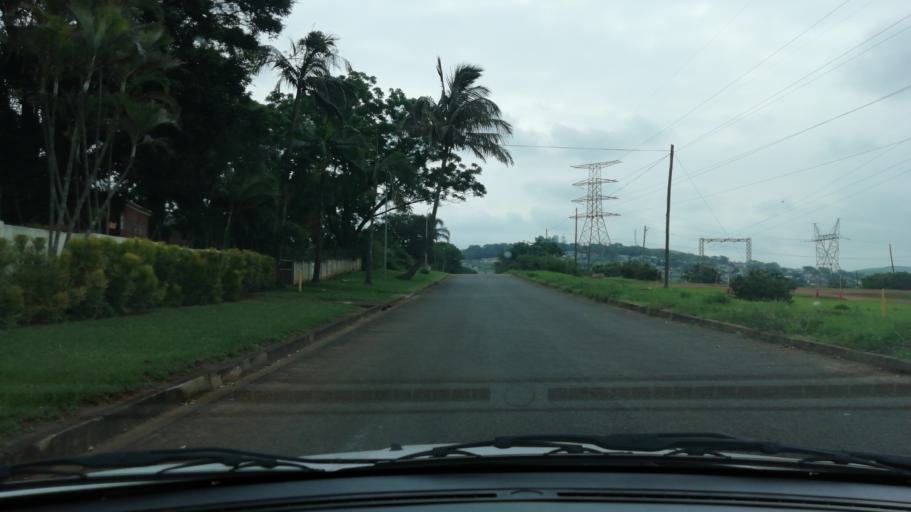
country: ZA
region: KwaZulu-Natal
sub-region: uThungulu District Municipality
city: Empangeni
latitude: -28.7378
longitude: 31.8882
